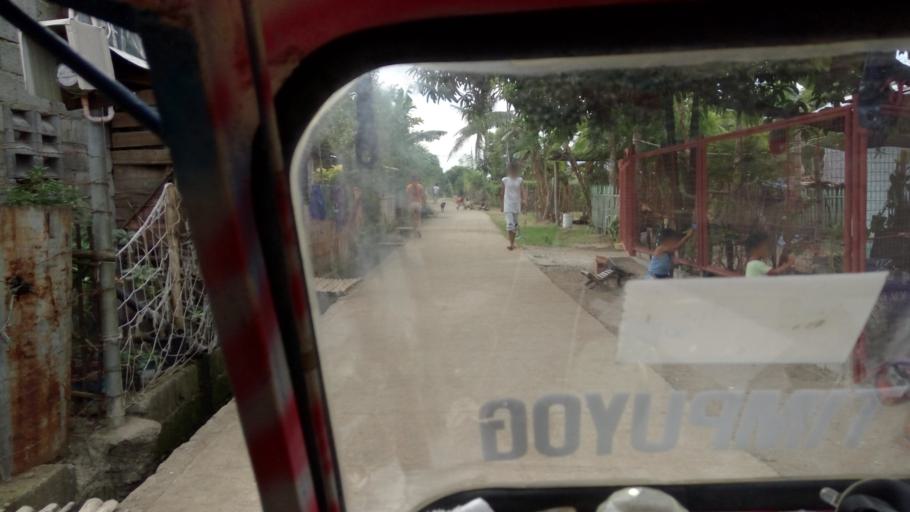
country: PH
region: Ilocos
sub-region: Province of La Union
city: Payocpoc Sur
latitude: 16.5055
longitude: 120.3328
